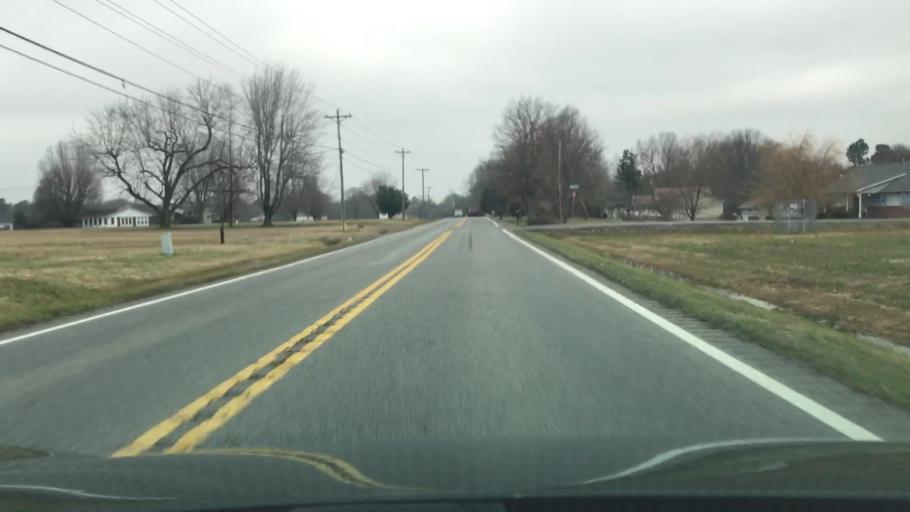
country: US
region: Kentucky
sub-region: Marshall County
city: Calvert City
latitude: 36.9533
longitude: -88.3704
